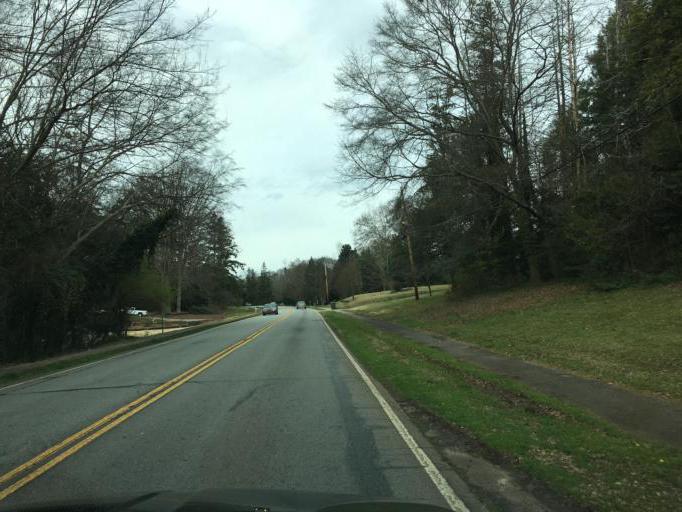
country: US
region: South Carolina
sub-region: Anderson County
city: Pendleton
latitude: 34.6681
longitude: -82.8031
